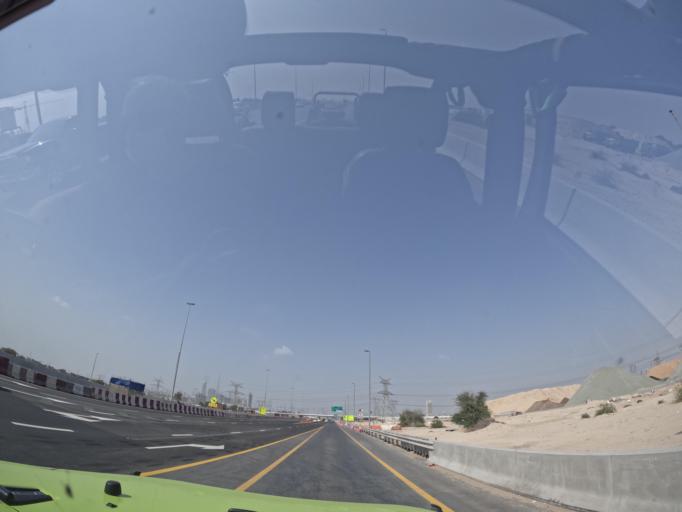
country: AE
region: Dubai
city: Dubai
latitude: 25.1649
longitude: 55.3289
